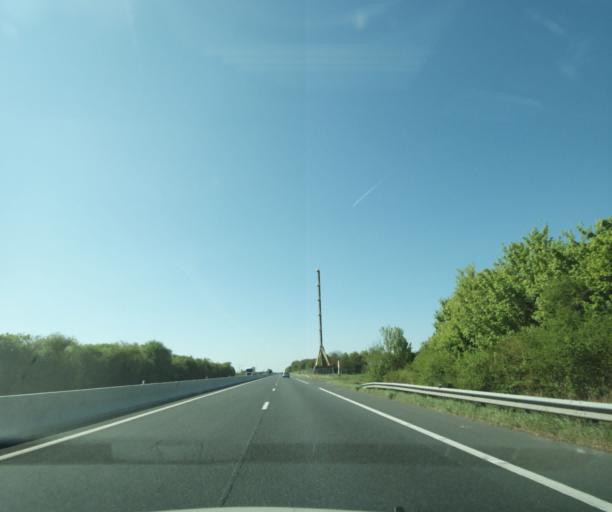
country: FR
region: Centre
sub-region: Departement du Cher
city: Massay
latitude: 47.1573
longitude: 1.9821
